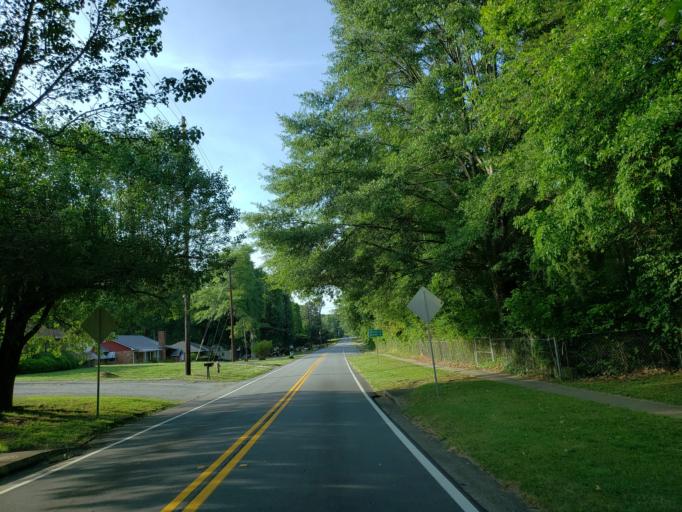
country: US
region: Georgia
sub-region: Carroll County
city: Bowdon
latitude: 33.5398
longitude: -85.2533
